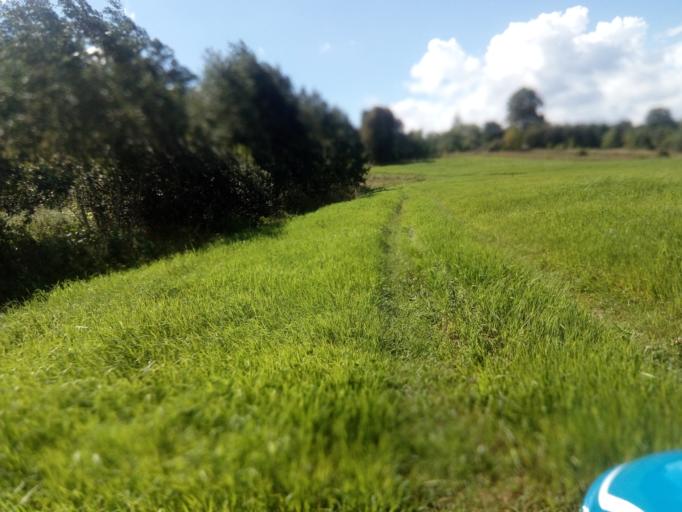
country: BY
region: Vitebsk
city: Dzisna
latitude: 55.6779
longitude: 28.3126
